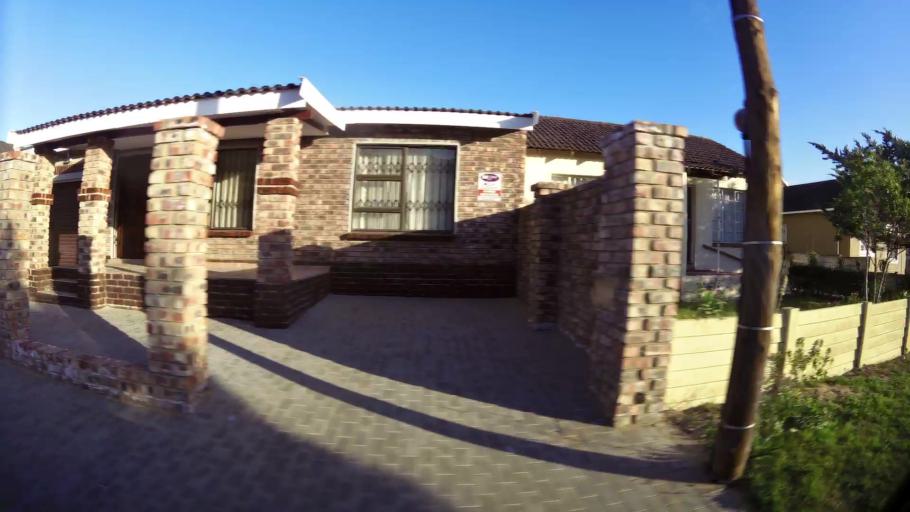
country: ZA
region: Western Cape
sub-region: Eden District Municipality
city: George
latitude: -34.0020
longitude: 22.6561
